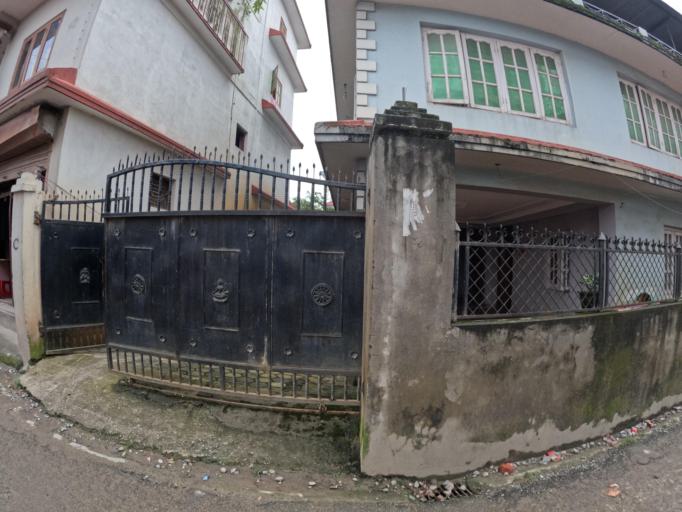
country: NP
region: Central Region
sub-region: Bagmati Zone
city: Kathmandu
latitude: 27.7464
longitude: 85.3200
